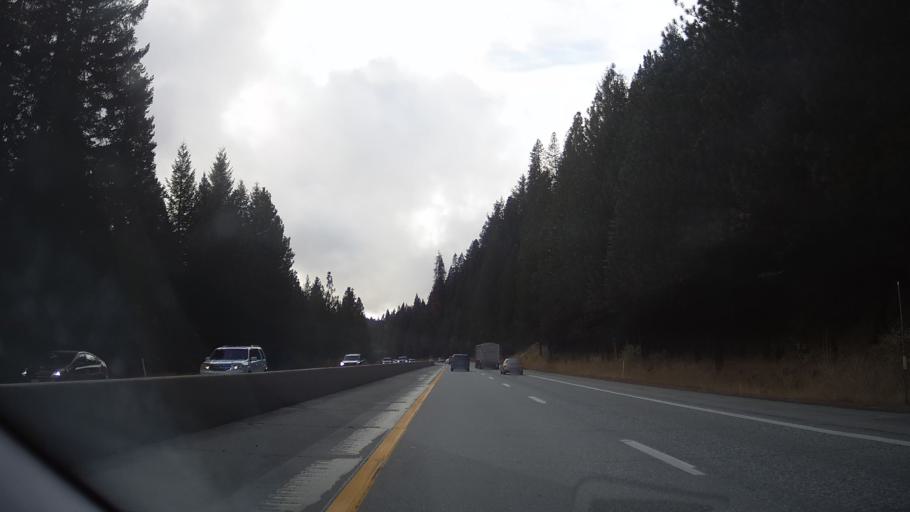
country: US
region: California
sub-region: Placer County
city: Foresthill
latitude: 39.2210
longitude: -120.7708
